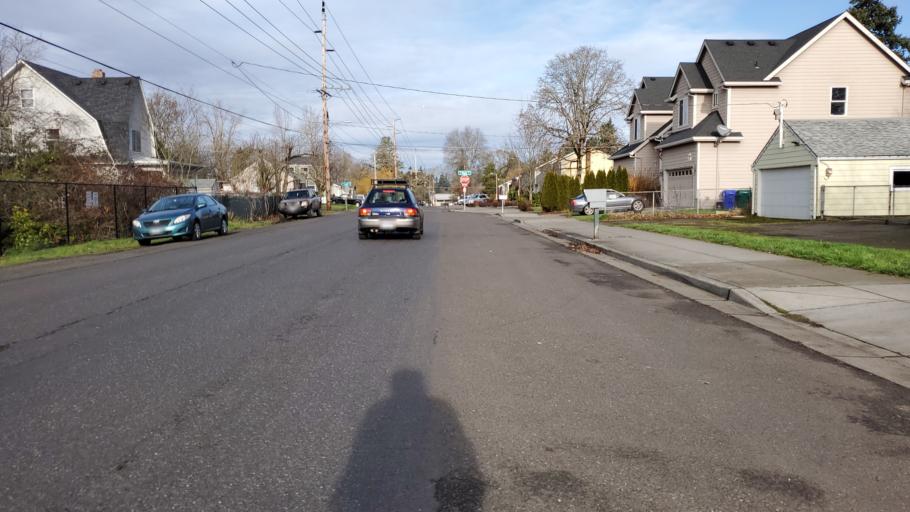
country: US
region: Oregon
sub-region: Clackamas County
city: Oak Grove
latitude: 45.4177
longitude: -122.6416
